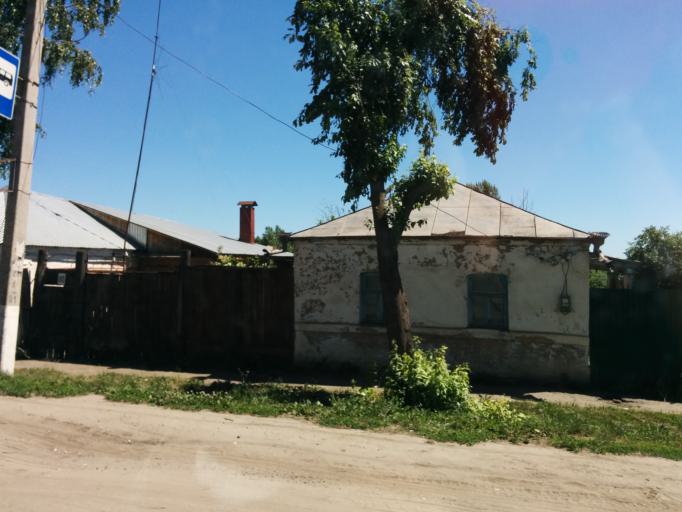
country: RU
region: Tambov
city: Morshansk
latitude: 53.4305
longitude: 41.7931
